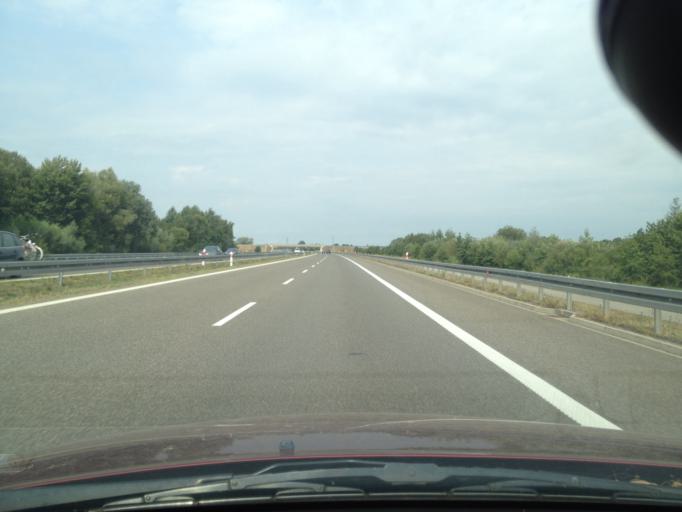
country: PL
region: West Pomeranian Voivodeship
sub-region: Powiat mysliborski
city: Nowogrodek Pomorski
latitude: 52.9367
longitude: 14.9792
